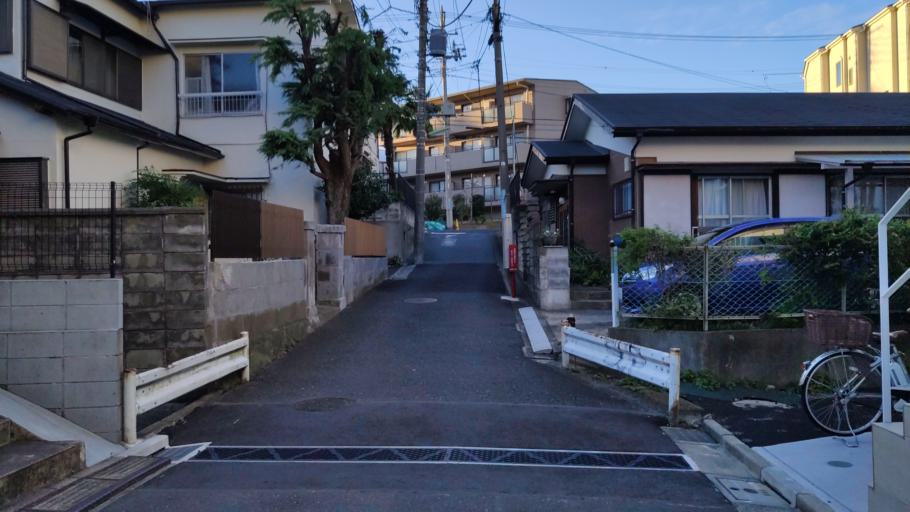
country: JP
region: Tokyo
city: Tokyo
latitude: 35.6337
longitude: 139.6546
